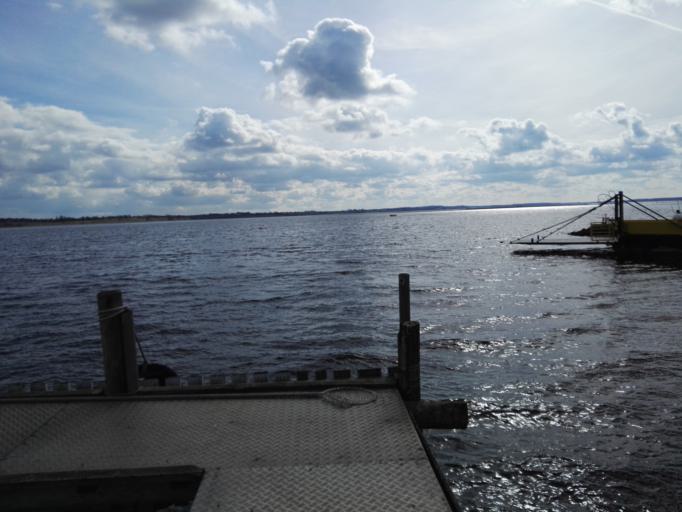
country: DK
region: Zealand
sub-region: Lejre Kommune
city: Ejby
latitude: 55.7572
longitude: 11.8365
